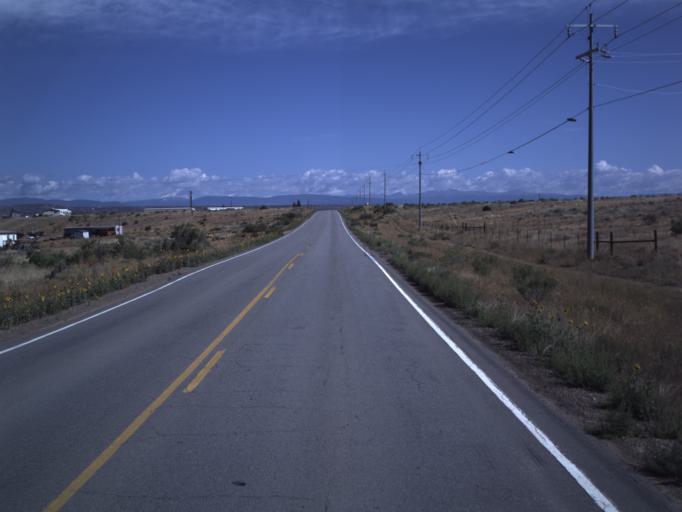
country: US
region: Utah
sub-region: Duchesne County
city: Duchesne
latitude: 40.2032
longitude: -110.3892
